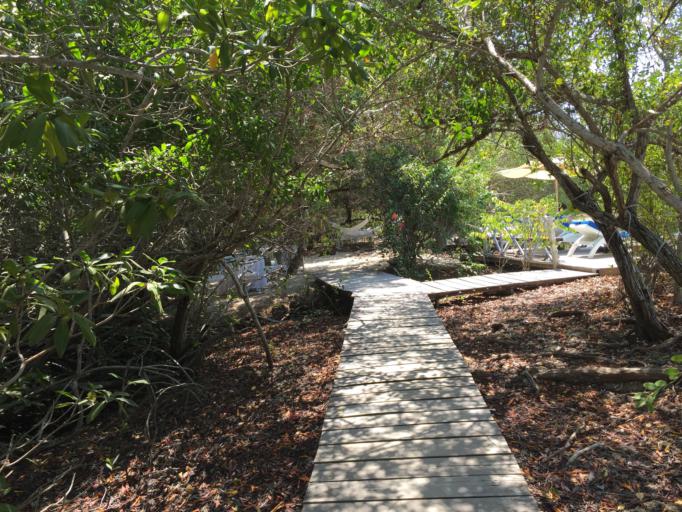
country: CO
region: Bolivar
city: Turbana
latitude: 10.1773
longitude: -75.7553
